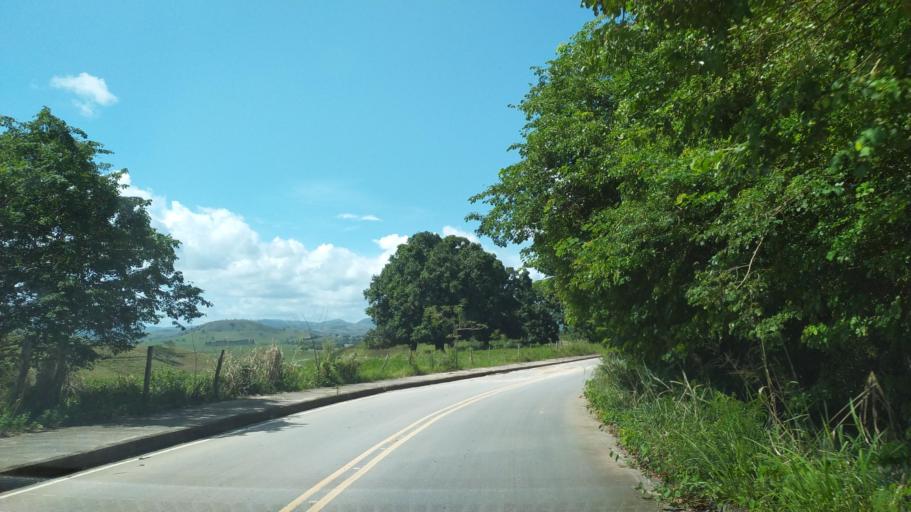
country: BR
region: Alagoas
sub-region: Uniao Dos Palmares
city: Uniao dos Palmares
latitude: -9.1685
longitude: -36.0613
